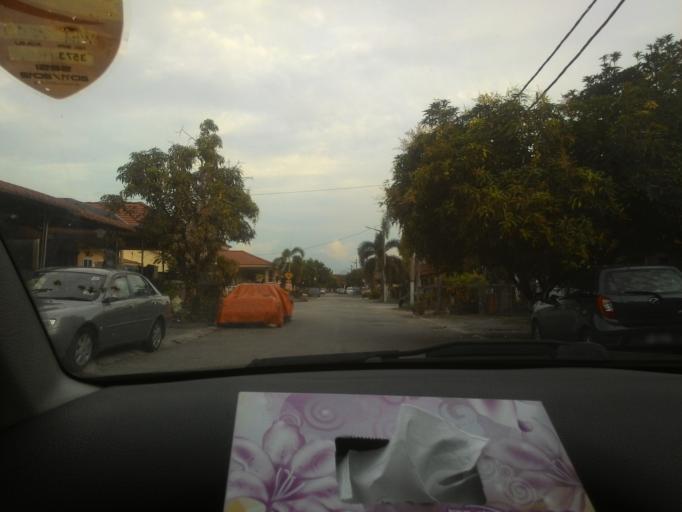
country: MY
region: Perak
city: Ipoh
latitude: 4.6781
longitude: 101.0808
